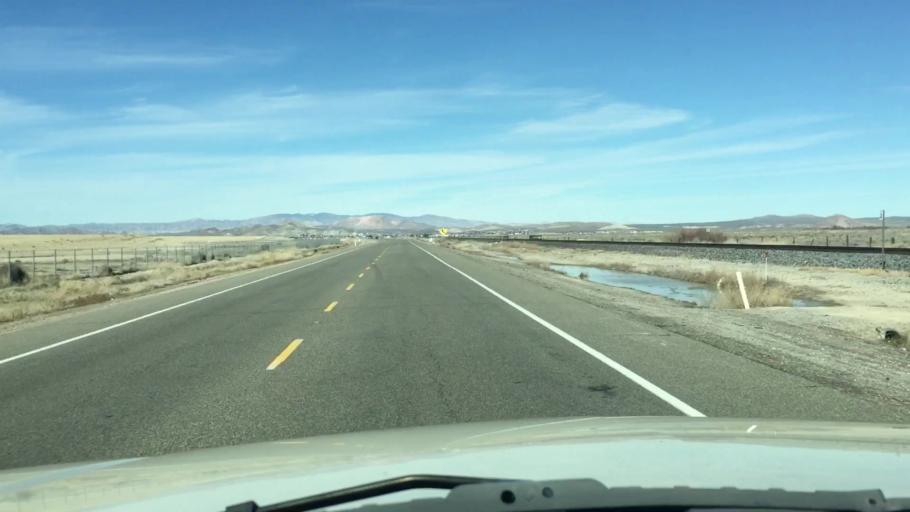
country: US
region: California
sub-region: Kern County
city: Rosamond
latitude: 34.7873
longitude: -118.1506
